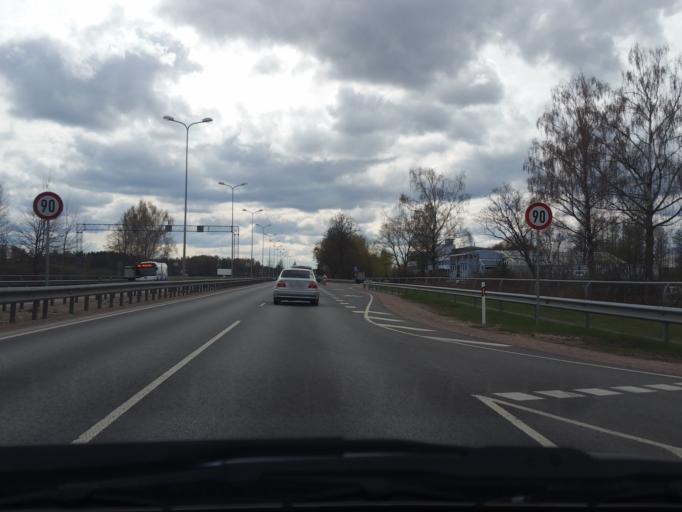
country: LV
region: Marupe
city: Marupe
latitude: 56.9277
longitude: 24.0037
